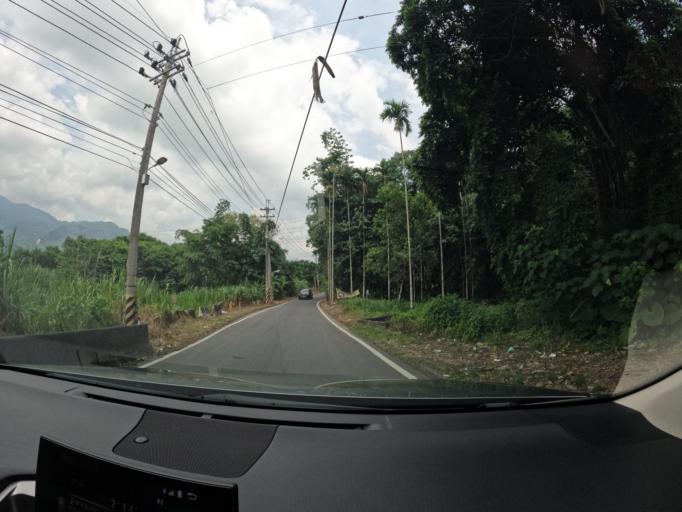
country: TW
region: Taiwan
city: Lugu
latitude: 23.8113
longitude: 120.8170
